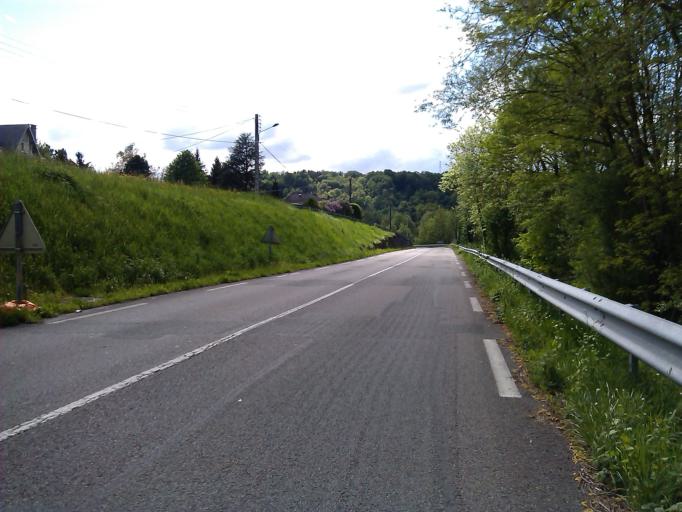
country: FR
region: Franche-Comte
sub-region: Departement du Doubs
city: Courcelles-les-Montbeliard
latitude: 47.5051
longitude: 6.7795
